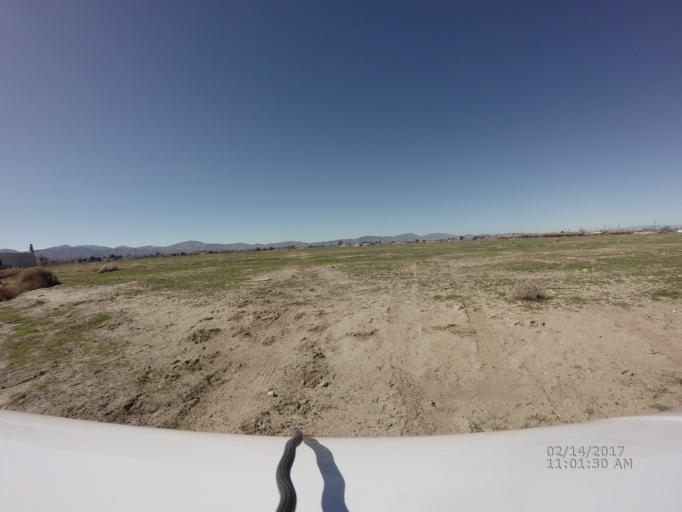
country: US
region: California
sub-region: Los Angeles County
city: Littlerock
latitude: 34.5706
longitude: -117.9522
